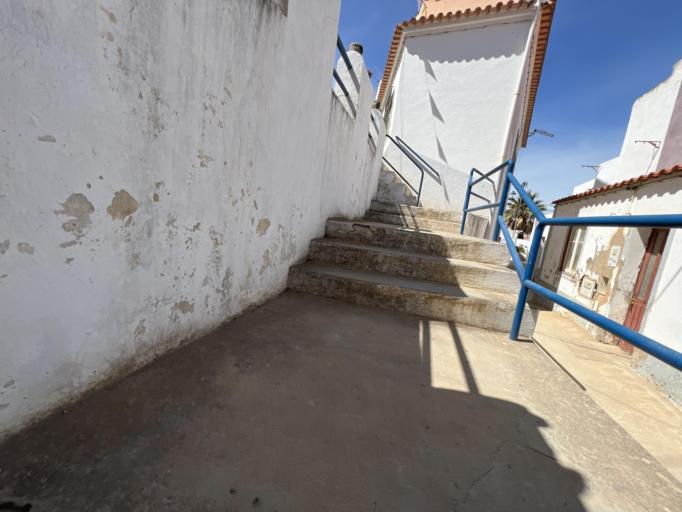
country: PT
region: Faro
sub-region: Portimao
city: Portimao
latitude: 37.1243
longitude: -8.5196
